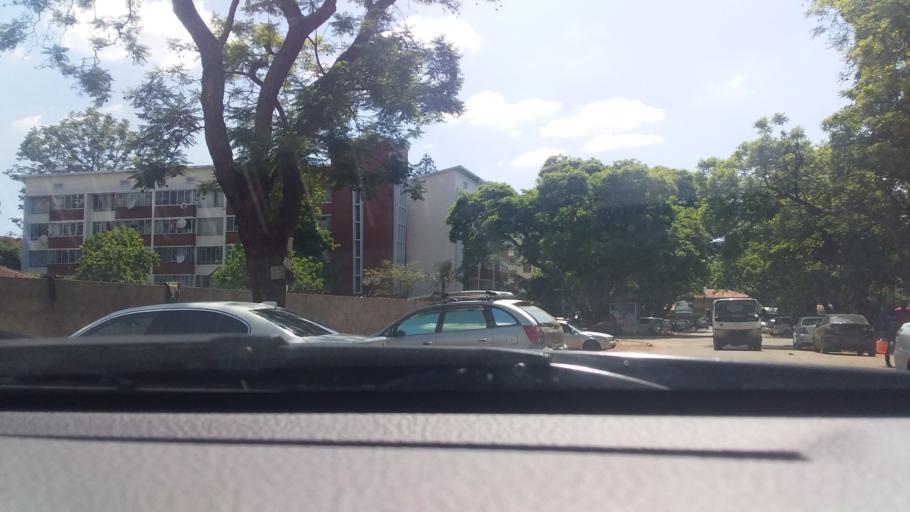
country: ZW
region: Harare
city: Harare
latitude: -17.8197
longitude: 31.0396
